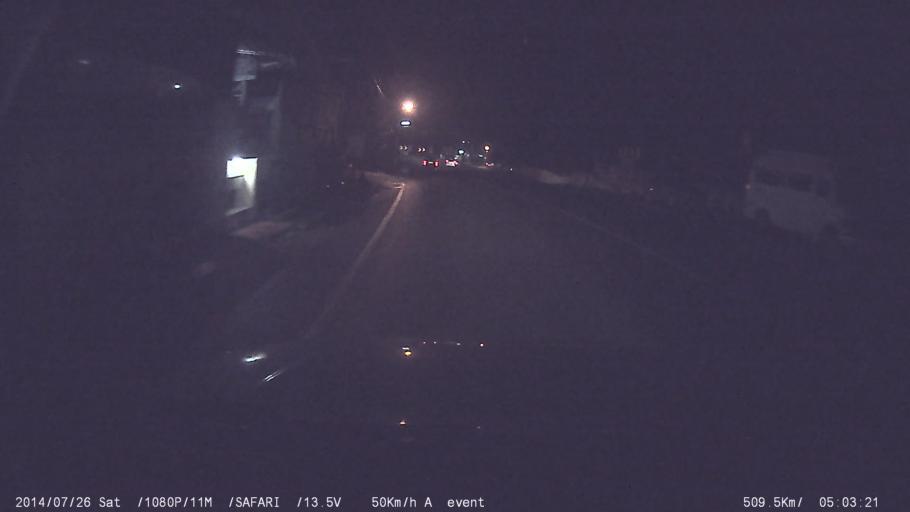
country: IN
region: Kerala
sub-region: Ernakulam
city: Perumbavoor
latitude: 10.1008
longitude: 76.4885
